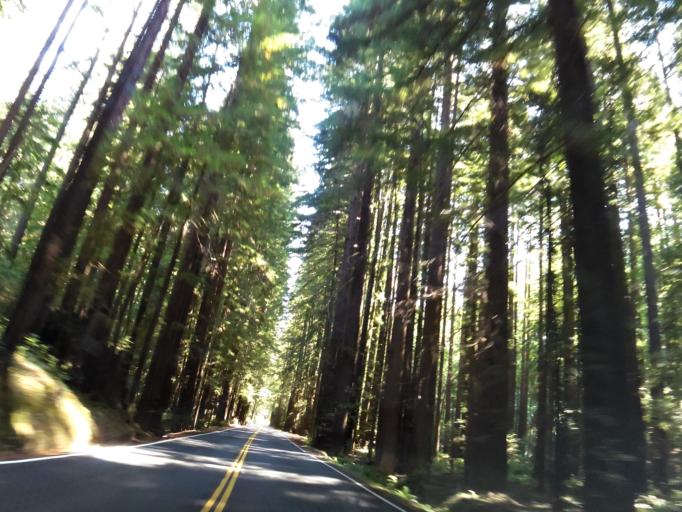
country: US
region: California
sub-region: Mendocino County
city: Boonville
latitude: 39.1563
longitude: -123.6058
